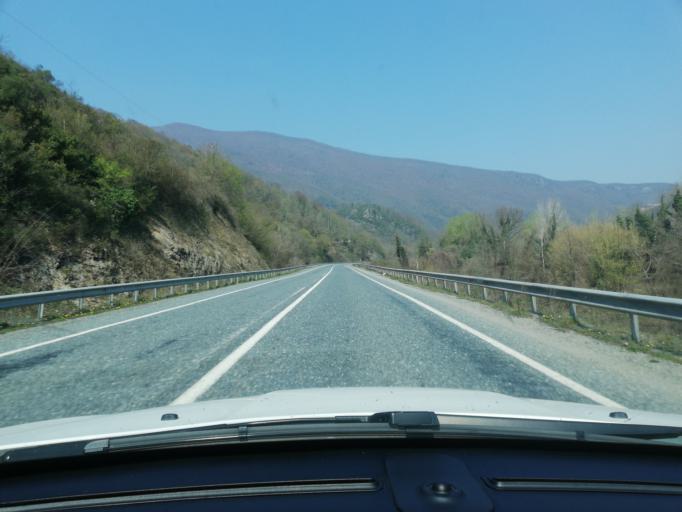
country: TR
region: Zonguldak
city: Gokcebey
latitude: 41.2560
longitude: 32.1601
